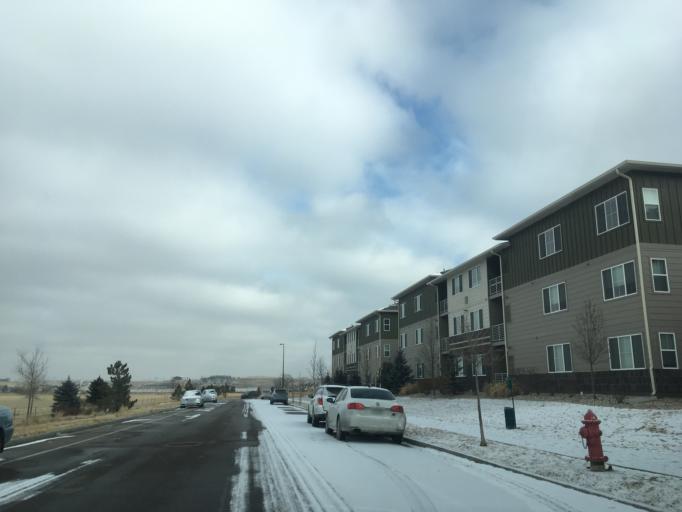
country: US
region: Colorado
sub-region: Boulder County
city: Lafayette
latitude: 39.9758
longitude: -105.0840
